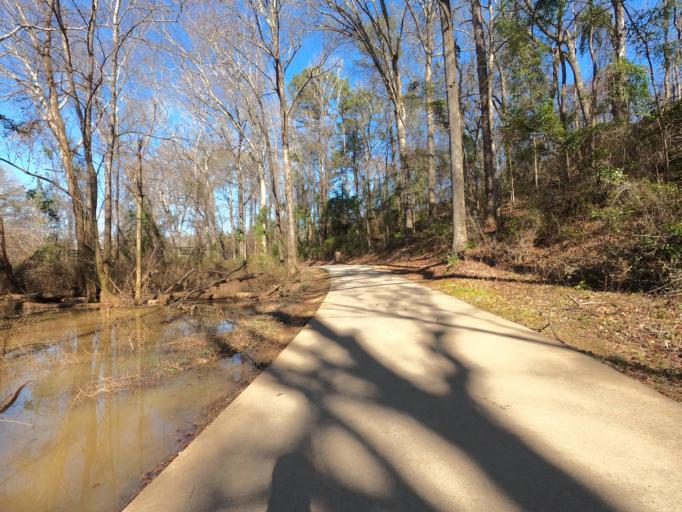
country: US
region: Georgia
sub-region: Clarke County
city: Athens
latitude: 33.9758
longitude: -83.3804
